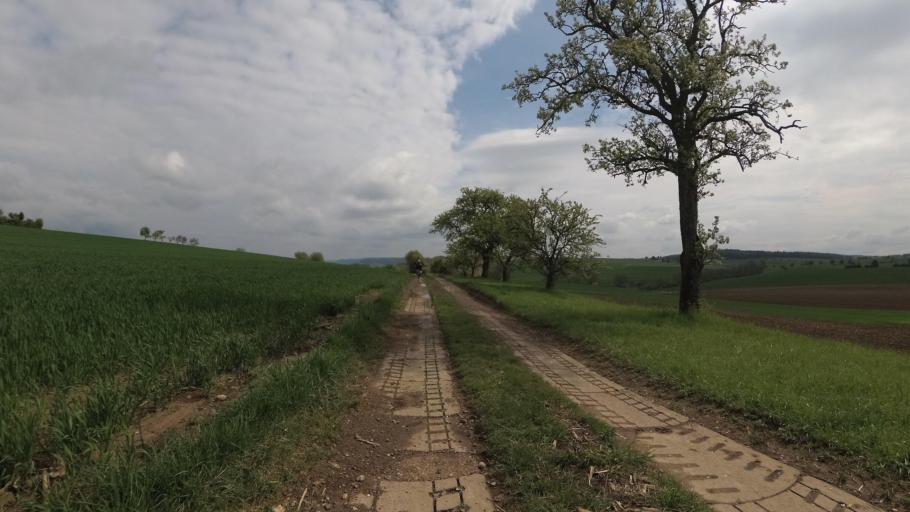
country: DE
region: Saarland
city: Merzig
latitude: 49.4058
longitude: 6.5857
